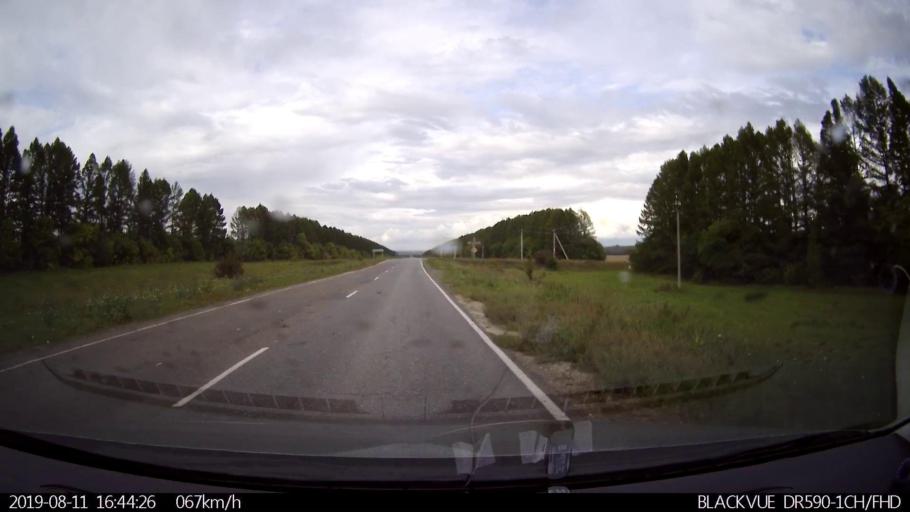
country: RU
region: Ulyanovsk
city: Mayna
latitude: 54.1789
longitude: 47.6798
